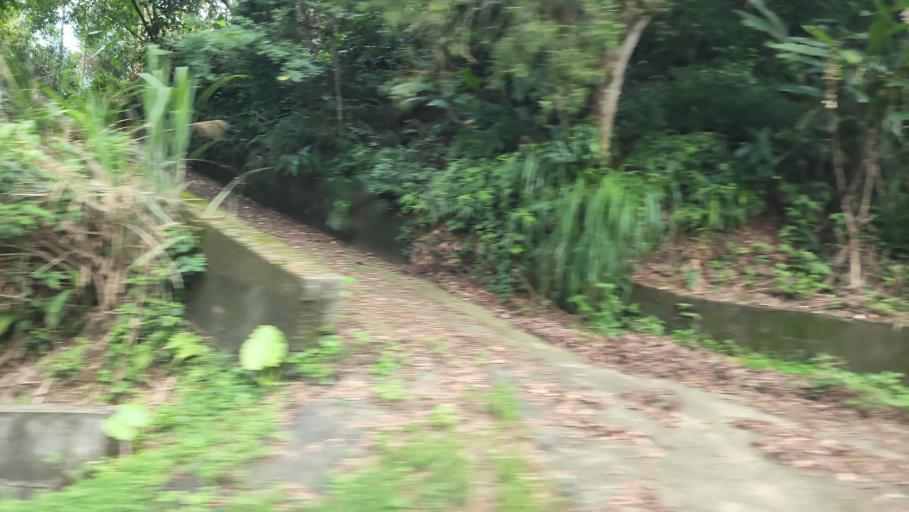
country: TW
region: Taiwan
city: Daxi
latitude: 24.8727
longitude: 121.4131
